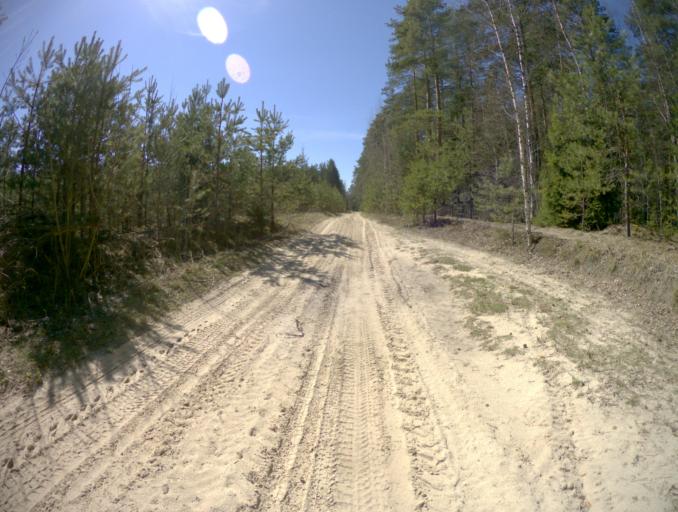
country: RU
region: Vladimir
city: Golovino
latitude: 55.9051
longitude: 40.4412
